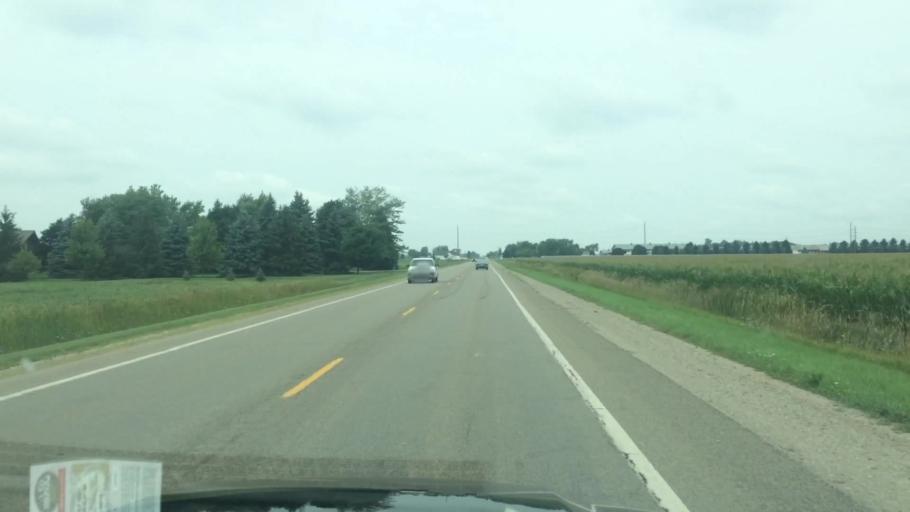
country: US
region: Michigan
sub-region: Huron County
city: Bad Axe
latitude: 43.8313
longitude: -83.0012
